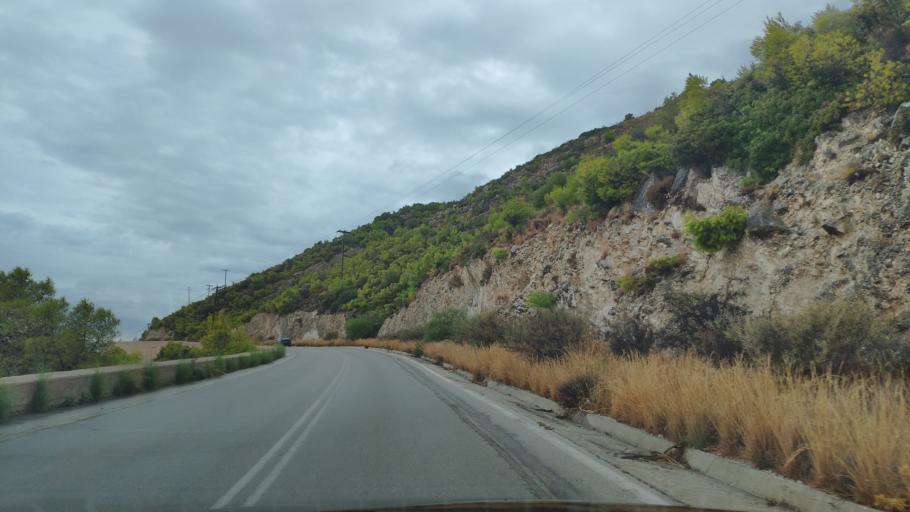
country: GR
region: Peloponnese
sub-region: Nomos Korinthias
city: Loutraki
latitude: 37.9830
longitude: 22.9747
